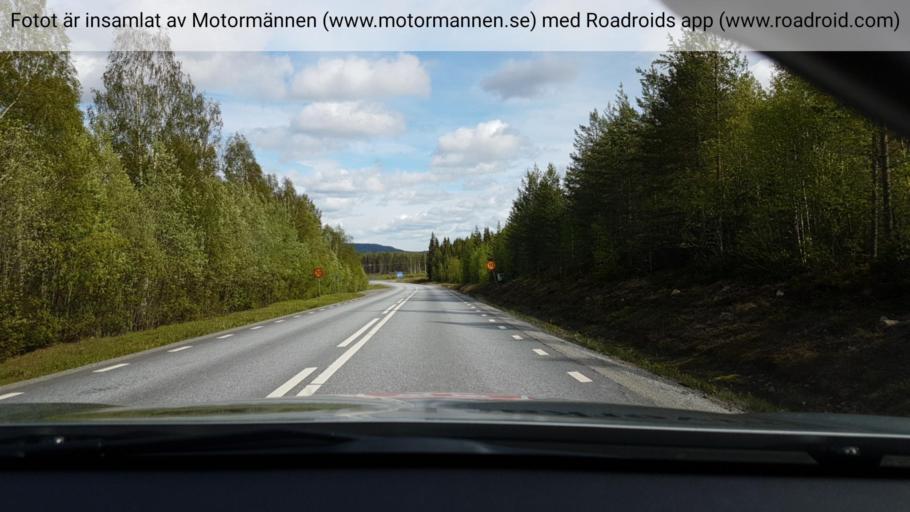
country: SE
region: Vaesterbotten
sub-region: Lycksele Kommun
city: Lycksele
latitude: 64.0702
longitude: 18.3899
